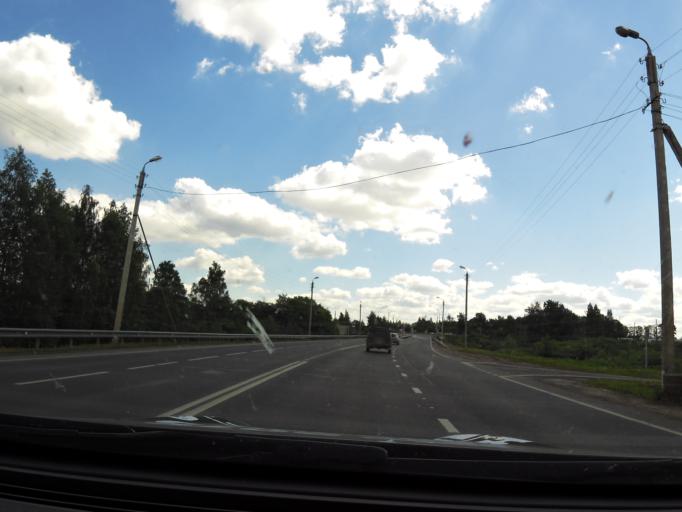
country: RU
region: Vologda
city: Vologda
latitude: 59.2414
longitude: 39.7886
